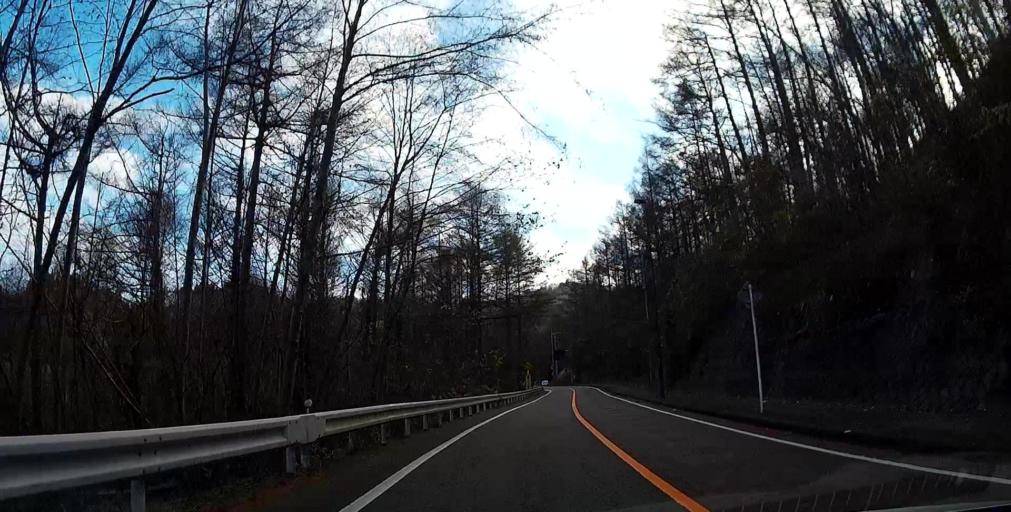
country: JP
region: Yamanashi
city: Fujikawaguchiko
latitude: 35.4768
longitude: 138.8350
